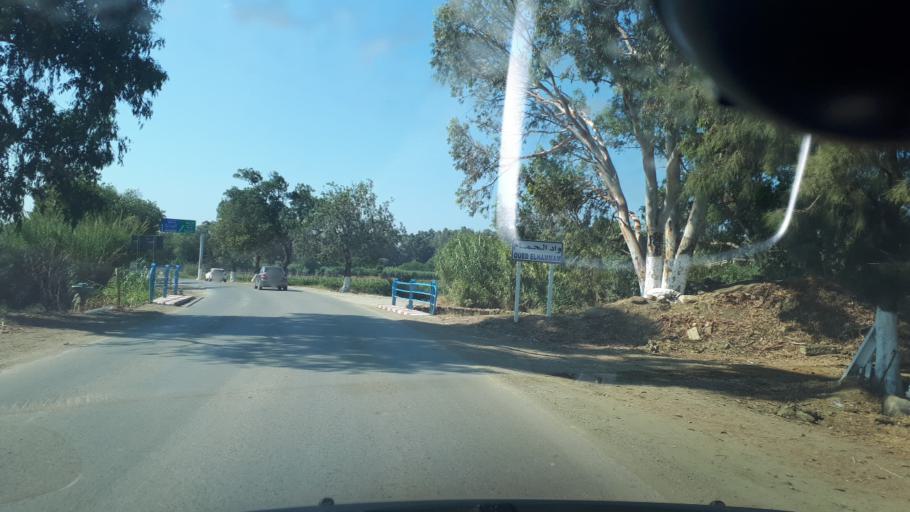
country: DZ
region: Boumerdes
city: Dellys
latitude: 36.8672
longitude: 3.8804
